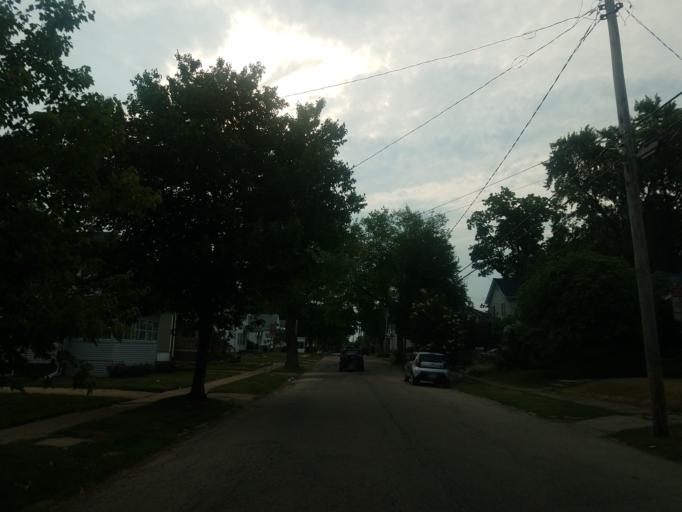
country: US
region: Illinois
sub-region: McLean County
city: Bloomington
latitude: 40.4728
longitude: -89.0007
